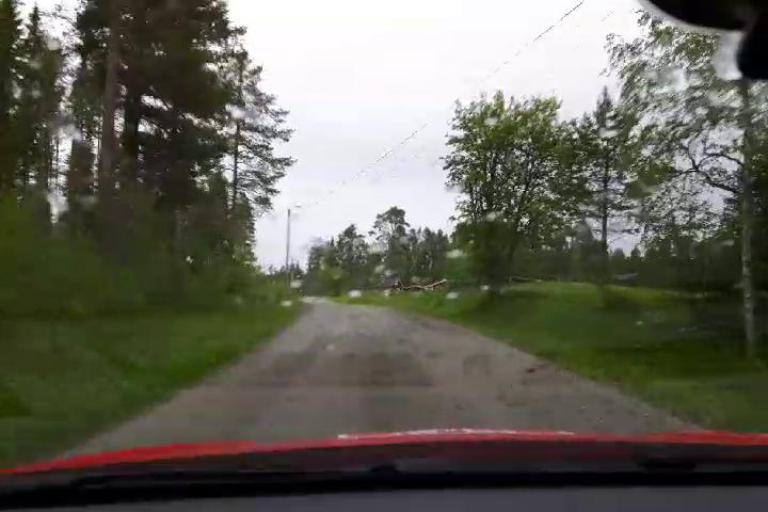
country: SE
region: Jaemtland
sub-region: Bergs Kommun
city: Hoverberg
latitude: 62.7444
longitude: 14.4555
